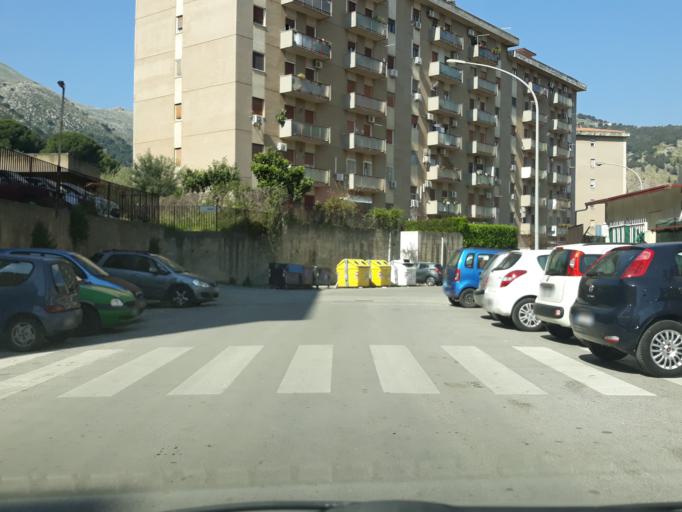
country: IT
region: Sicily
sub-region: Palermo
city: Piano dei Geli
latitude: 38.1248
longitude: 13.2924
